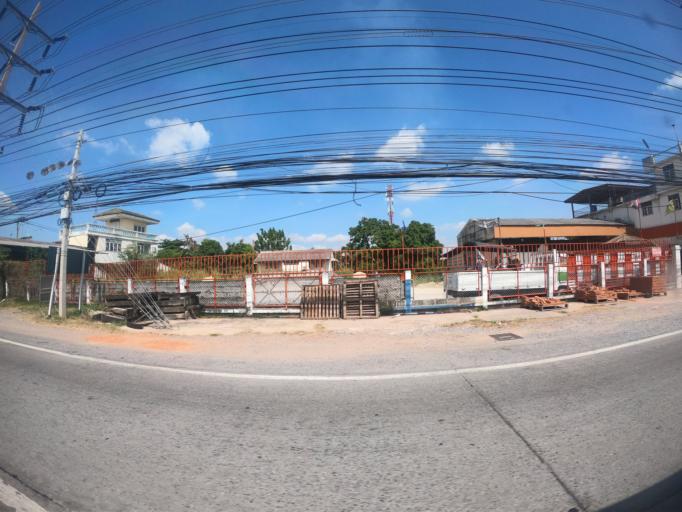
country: TH
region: Nakhon Ratchasima
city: Nakhon Ratchasima
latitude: 14.9589
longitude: 102.0484
